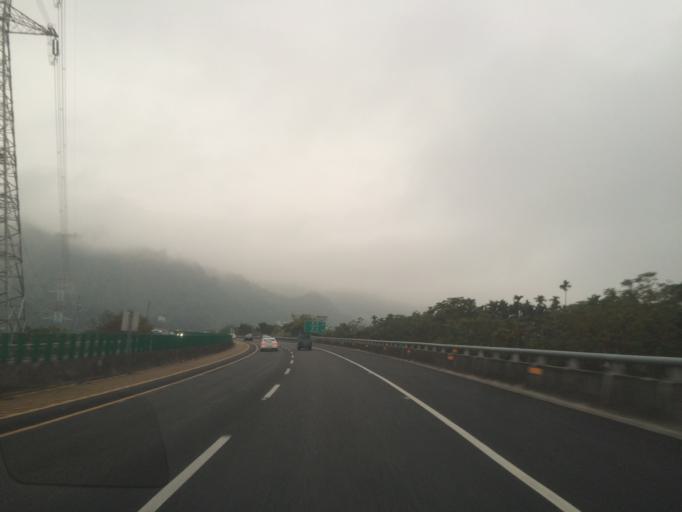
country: TW
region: Taiwan
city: Zhongxing New Village
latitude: 23.9966
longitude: 120.8015
